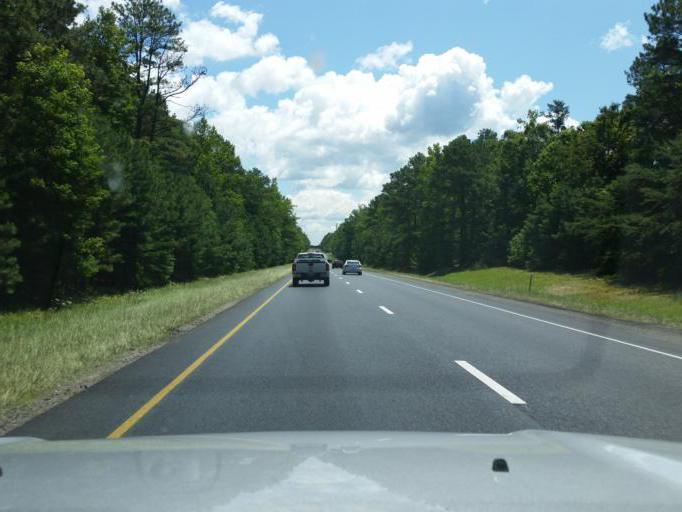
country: US
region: Virginia
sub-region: New Kent County
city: New Kent
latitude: 37.5064
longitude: -77.0986
